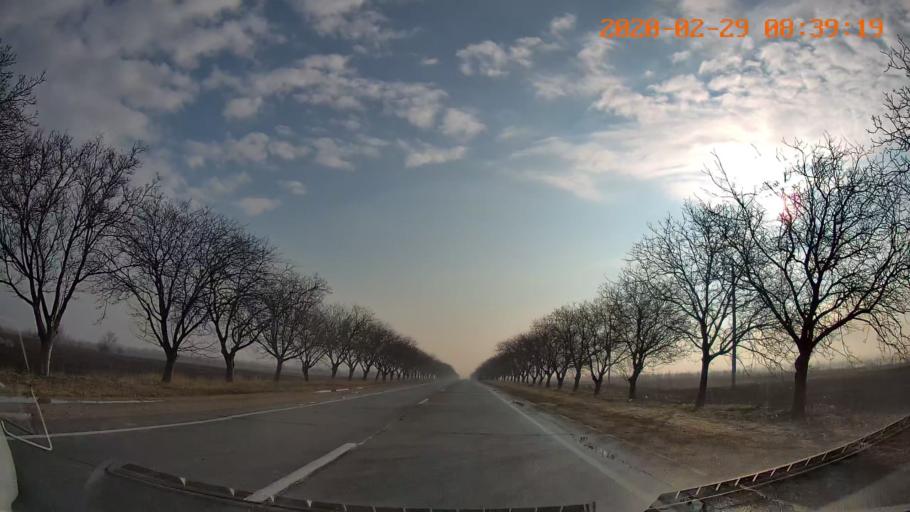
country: MD
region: Anenii Noi
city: Varnita
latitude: 46.9224
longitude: 29.3954
